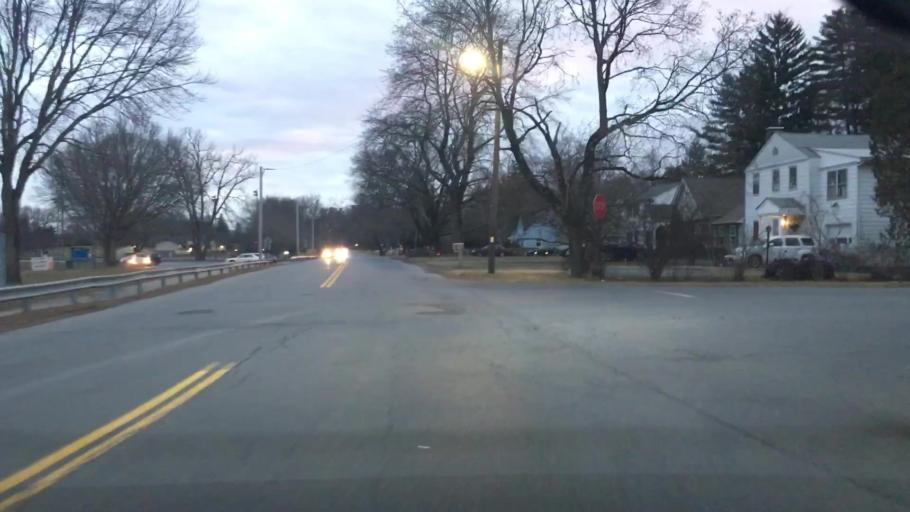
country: US
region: New York
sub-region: Dutchess County
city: Spackenkill
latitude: 41.6760
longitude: -73.9129
